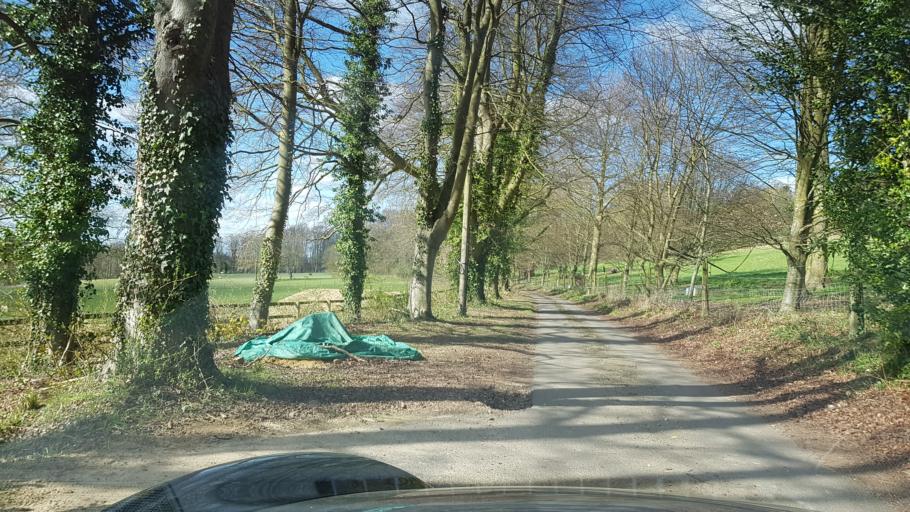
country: GB
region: England
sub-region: Surrey
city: Godalming
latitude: 51.2253
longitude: -0.6336
